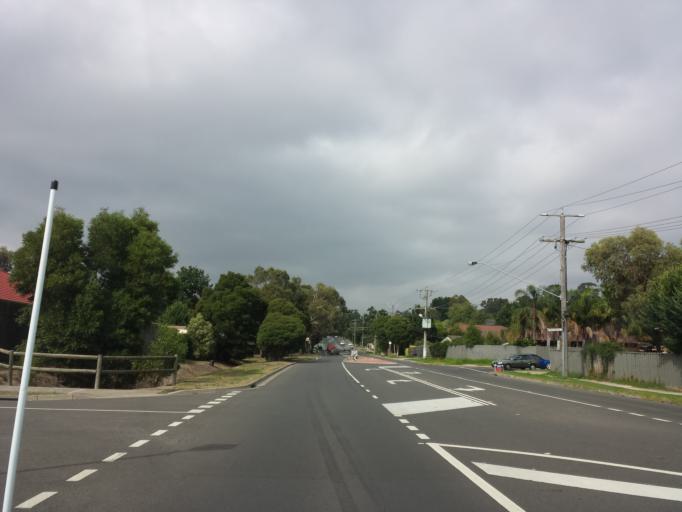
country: AU
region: Victoria
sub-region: Maroondah
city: Bayswater North
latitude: -37.8259
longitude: 145.3035
